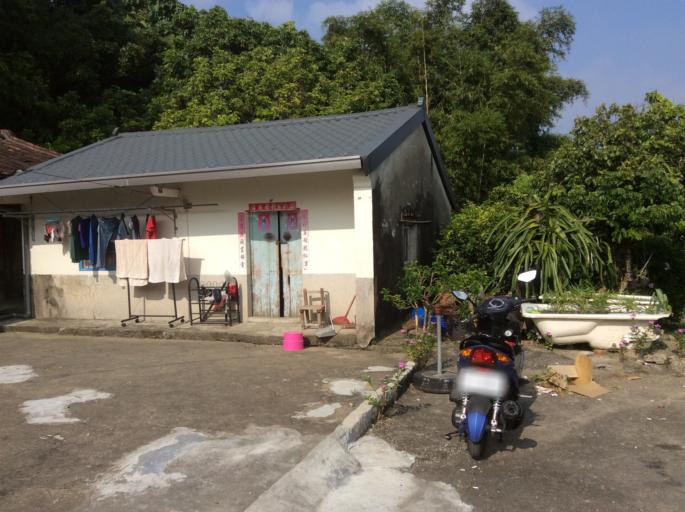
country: TW
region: Taiwan
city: Yujing
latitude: 22.9970
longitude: 120.4136
